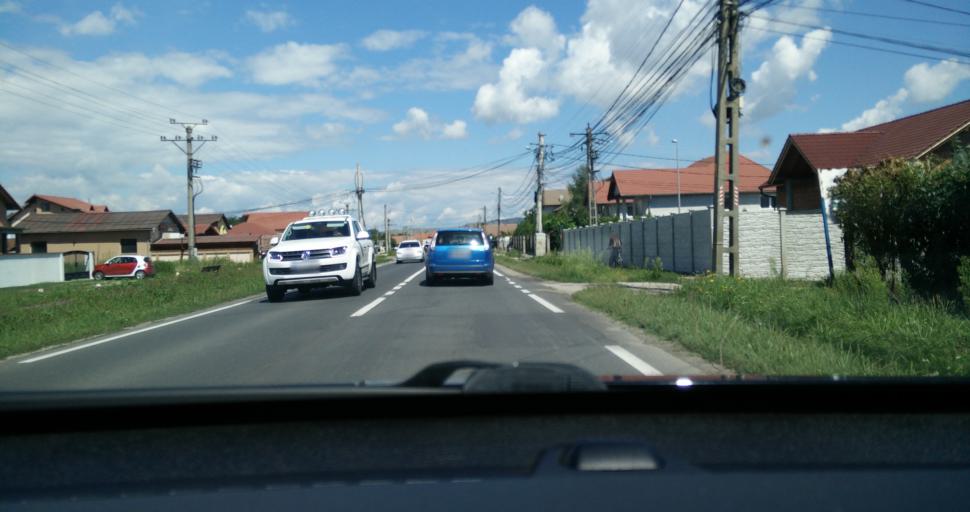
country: RO
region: Alba
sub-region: Municipiul Sebes
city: Sebes
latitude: 45.9406
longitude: 23.5631
